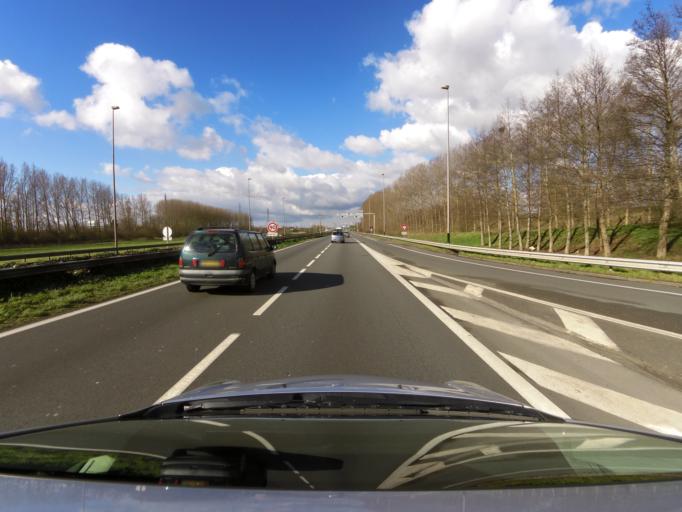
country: FR
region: Nord-Pas-de-Calais
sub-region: Departement du Nord
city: Grande-Synthe
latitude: 51.0019
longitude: 2.2981
